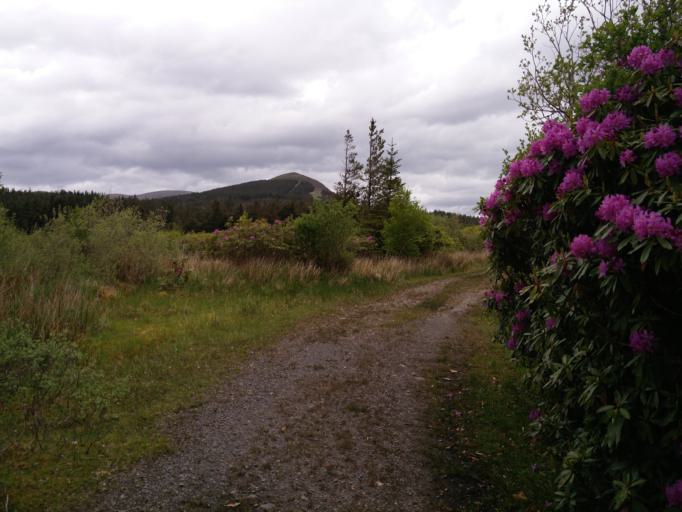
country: IE
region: Connaught
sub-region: Maigh Eo
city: Westport
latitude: 53.9871
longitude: -9.5723
